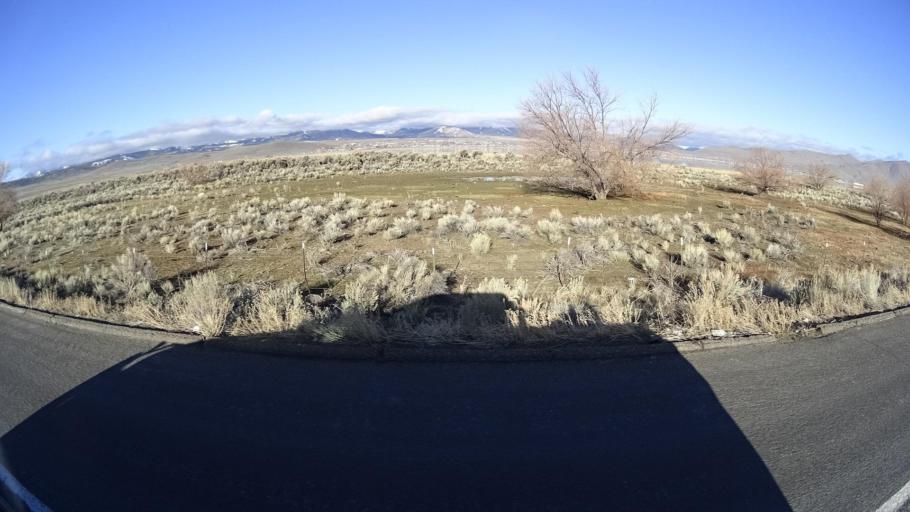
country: US
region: Nevada
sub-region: Washoe County
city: Cold Springs
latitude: 39.6534
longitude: -119.9586
